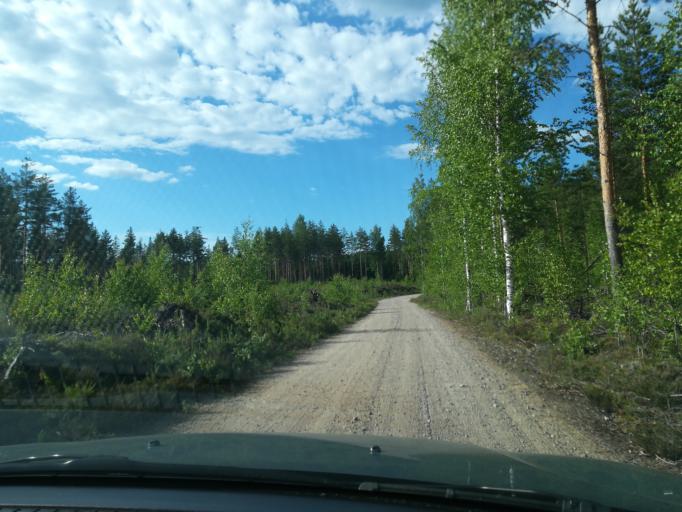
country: FI
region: Southern Savonia
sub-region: Savonlinna
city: Savonlinna
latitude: 61.6431
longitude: 28.7173
